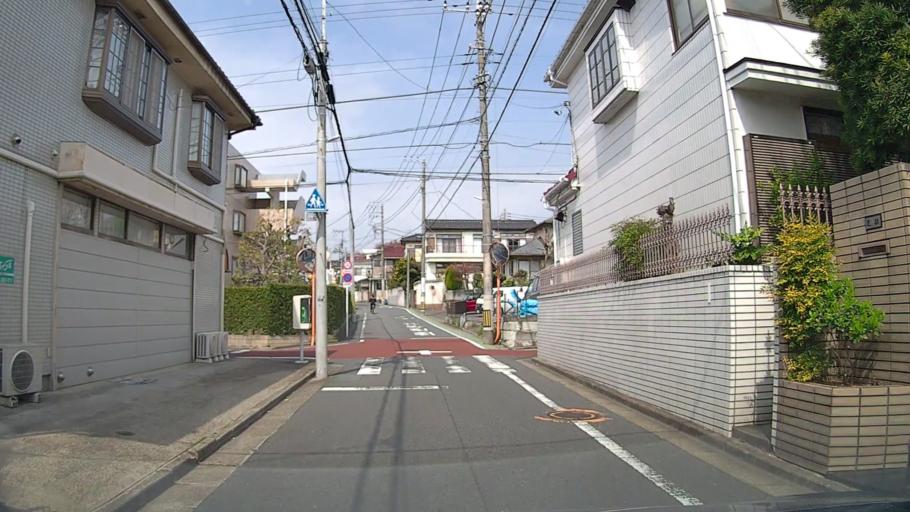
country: JP
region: Saitama
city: Wako
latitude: 35.7600
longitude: 139.5931
